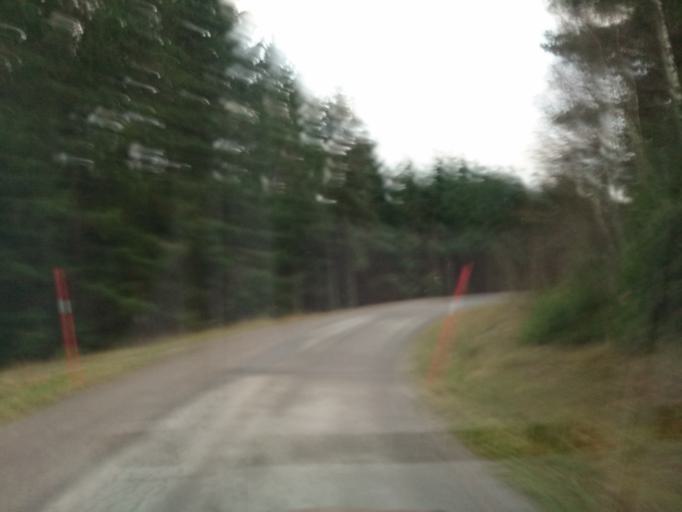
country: SE
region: OEstergoetland
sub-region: Atvidabergs Kommun
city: Atvidaberg
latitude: 58.3257
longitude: 16.1077
